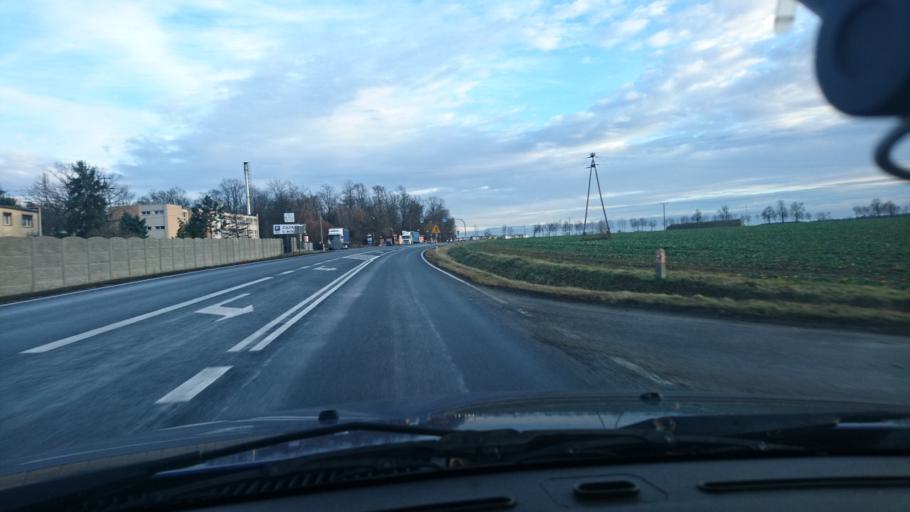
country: PL
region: Greater Poland Voivodeship
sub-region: Powiat kepinski
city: Slupia pod Kepnem
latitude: 51.2418
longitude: 18.0316
